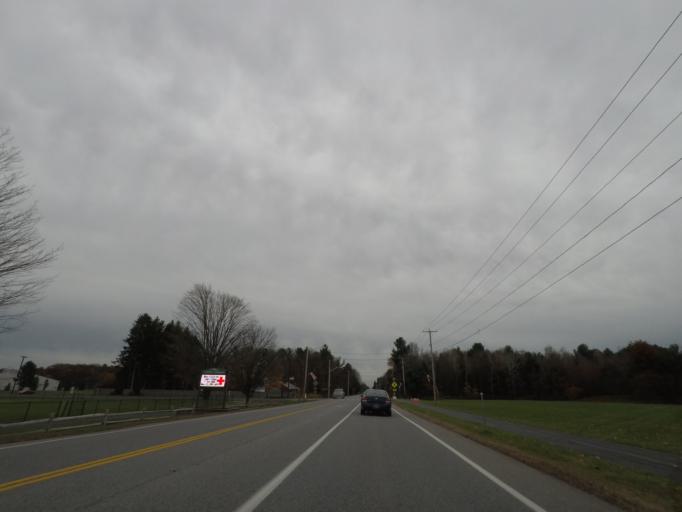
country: US
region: New York
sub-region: Saratoga County
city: Country Knolls
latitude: 42.8637
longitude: -73.8204
